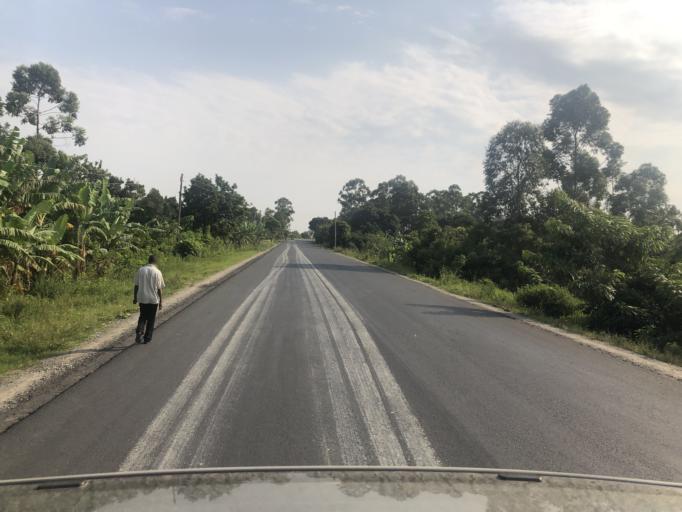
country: UG
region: Western Region
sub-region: Rubirizi District
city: Rubirizi
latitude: -0.2289
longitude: 30.0940
